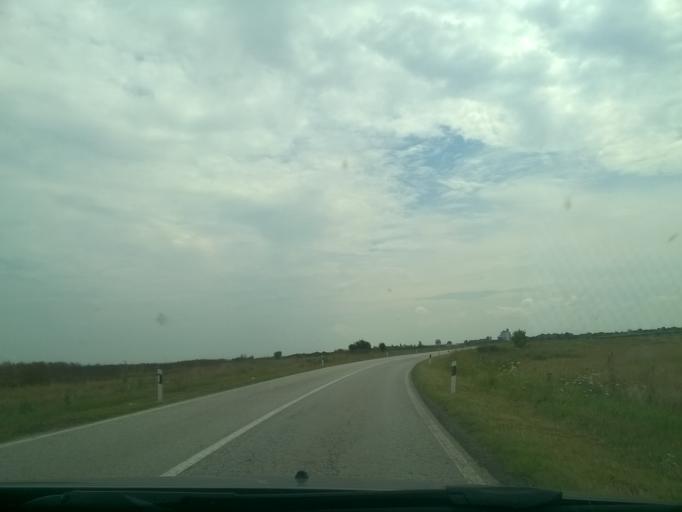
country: RS
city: Konak
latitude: 45.3292
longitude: 20.8959
